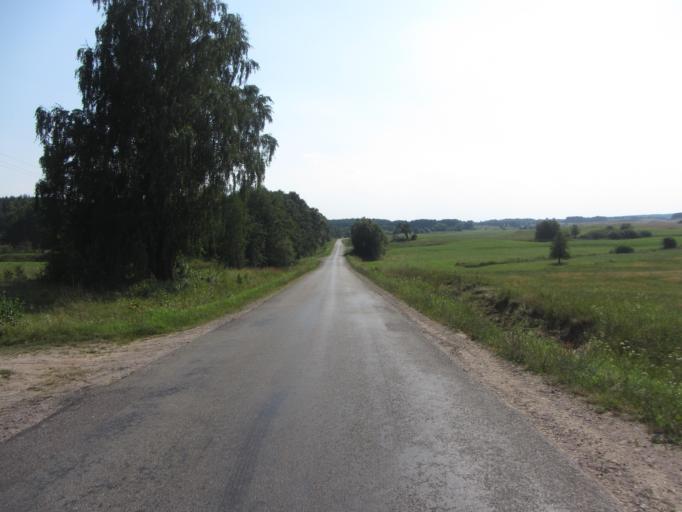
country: LT
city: Veisiejai
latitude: 54.2061
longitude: 23.7741
